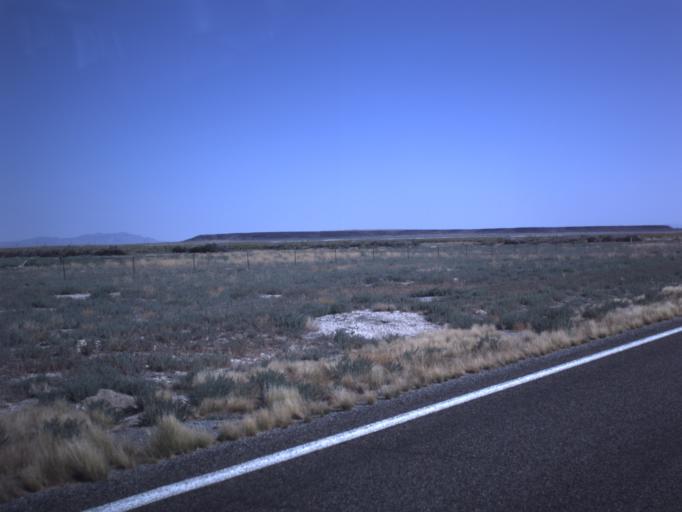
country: US
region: Utah
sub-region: Millard County
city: Delta
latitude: 39.1175
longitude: -112.7402
